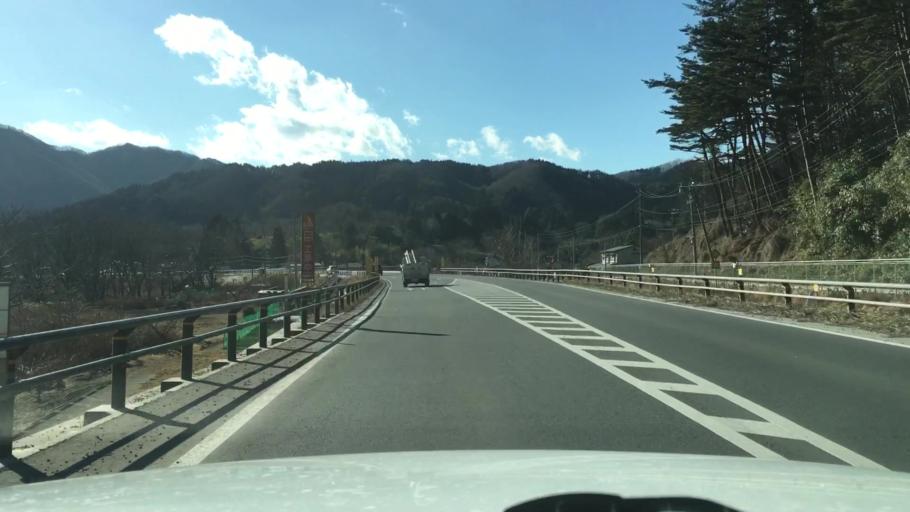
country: JP
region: Iwate
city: Miyako
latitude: 39.6349
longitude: 141.8422
